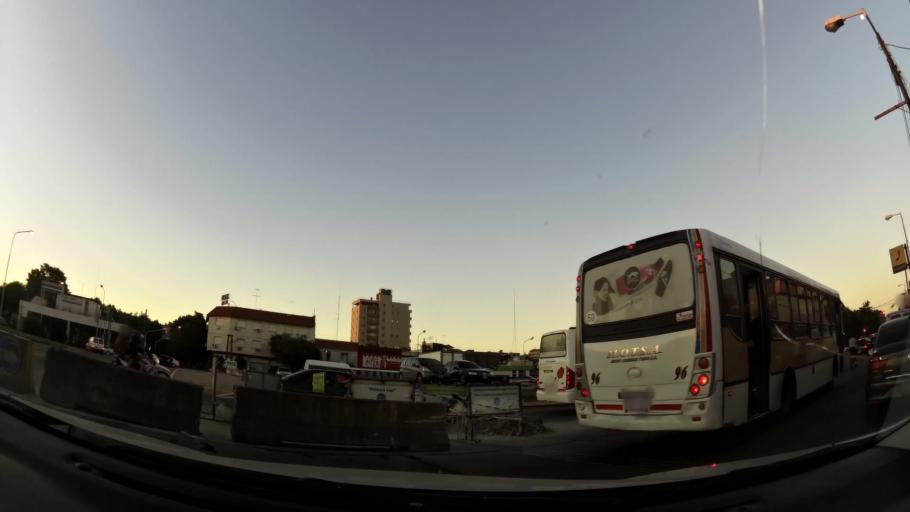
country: AR
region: Buenos Aires
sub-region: Partido de Tigre
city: Tigre
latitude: -34.4354
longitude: -58.5669
